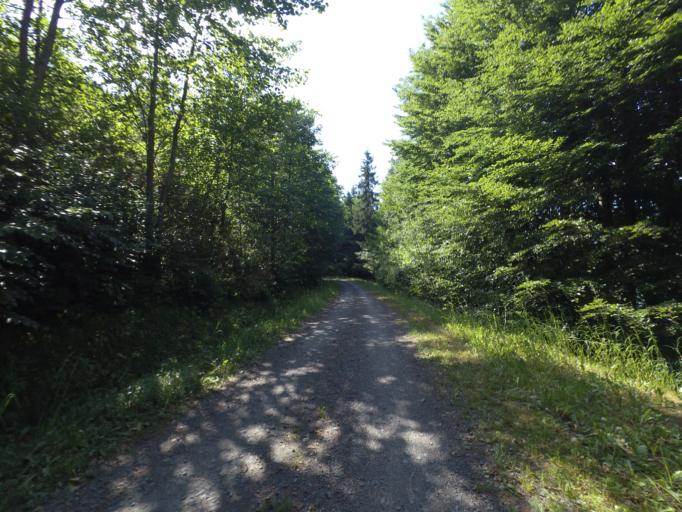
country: AT
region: Carinthia
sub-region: Politischer Bezirk Spittal an der Drau
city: Millstatt
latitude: 46.7880
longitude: 13.5855
